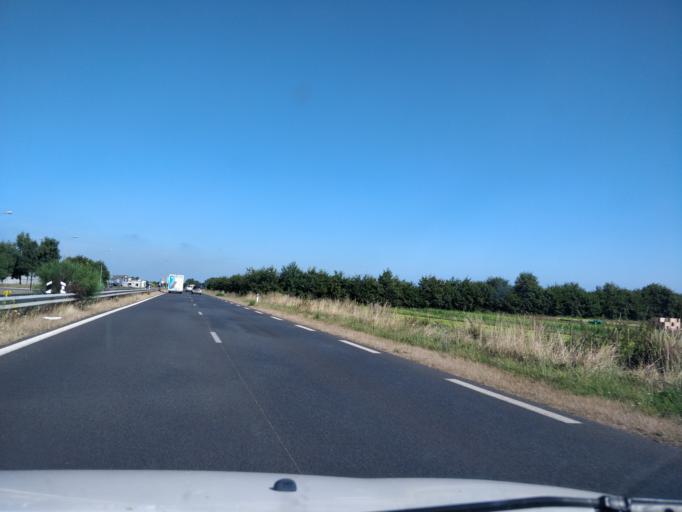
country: FR
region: Brittany
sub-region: Departement des Cotes-d'Armor
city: Pordic
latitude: 48.5571
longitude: -2.8072
